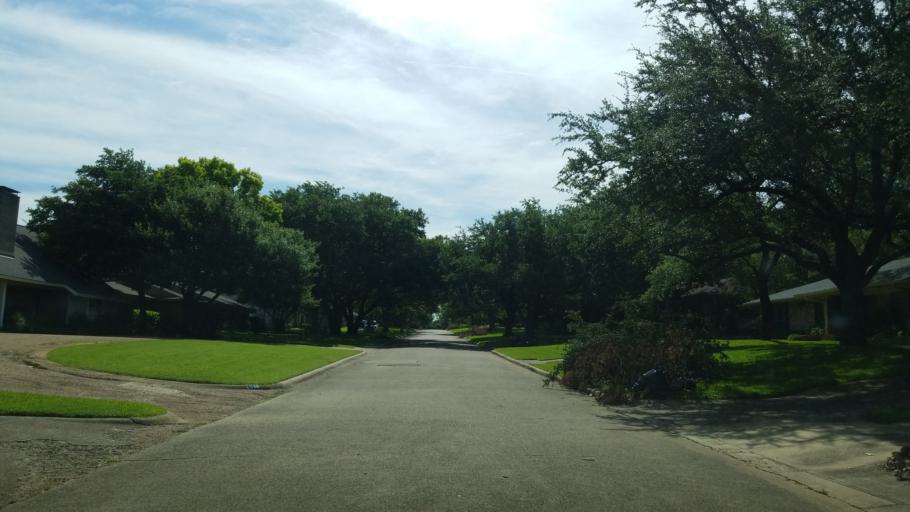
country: US
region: Texas
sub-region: Dallas County
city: Addison
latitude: 32.9063
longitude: -96.8358
